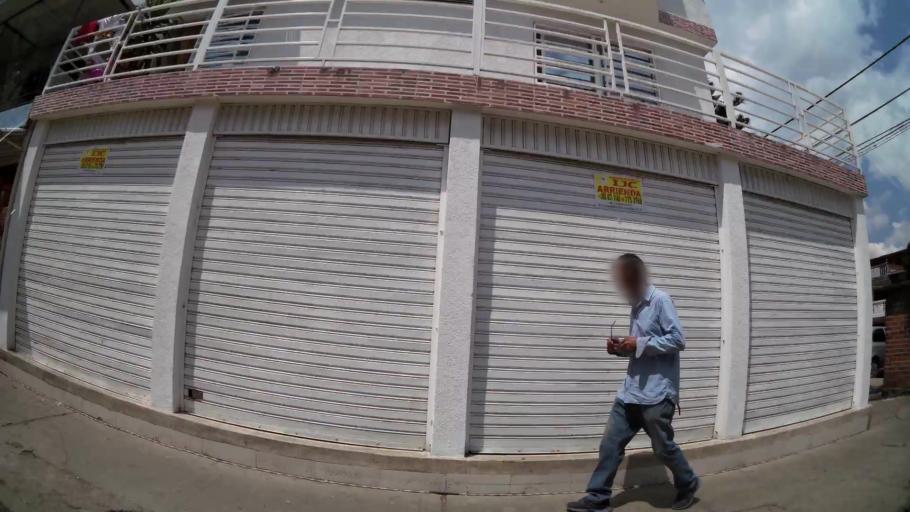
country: CO
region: Valle del Cauca
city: Cali
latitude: 3.4877
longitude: -76.4848
